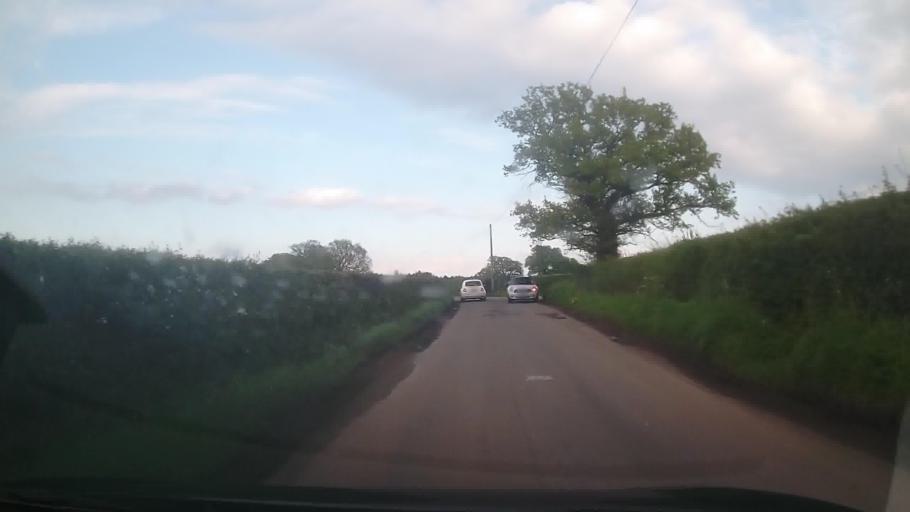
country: GB
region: England
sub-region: Shropshire
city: Ellesmere
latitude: 52.9382
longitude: -2.8790
